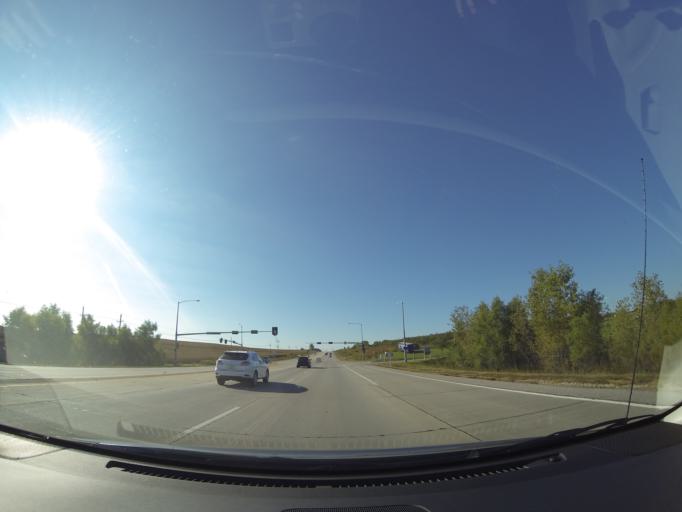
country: US
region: Nebraska
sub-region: Sarpy County
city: Gretna
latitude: 41.1985
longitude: -96.2344
